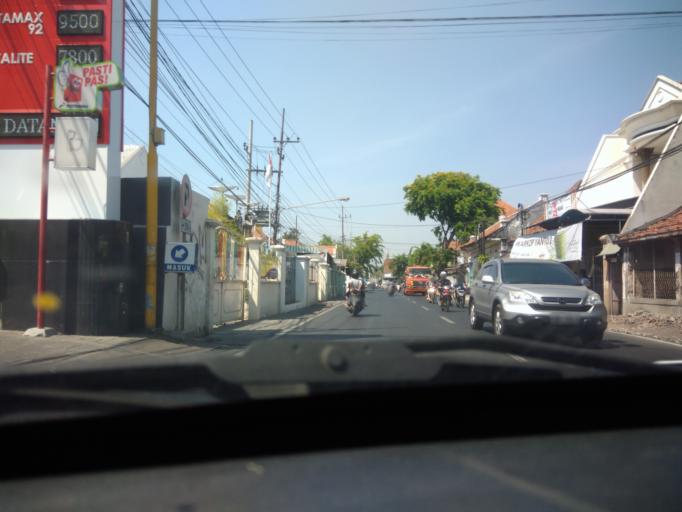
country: ID
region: East Java
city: Gubengairlangga
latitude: -7.2863
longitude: 112.7452
